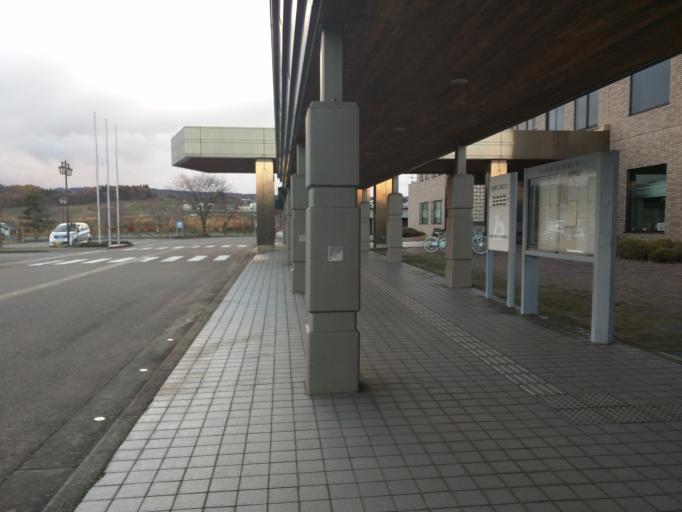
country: JP
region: Fukushima
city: Kitakata
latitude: 37.5112
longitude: 139.8298
